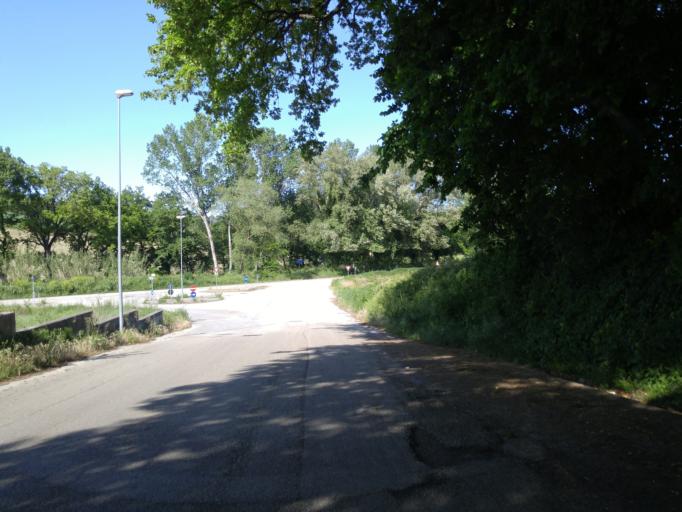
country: IT
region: The Marches
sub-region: Provincia di Pesaro e Urbino
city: Mombaroccio
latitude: 43.8331
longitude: 12.8653
